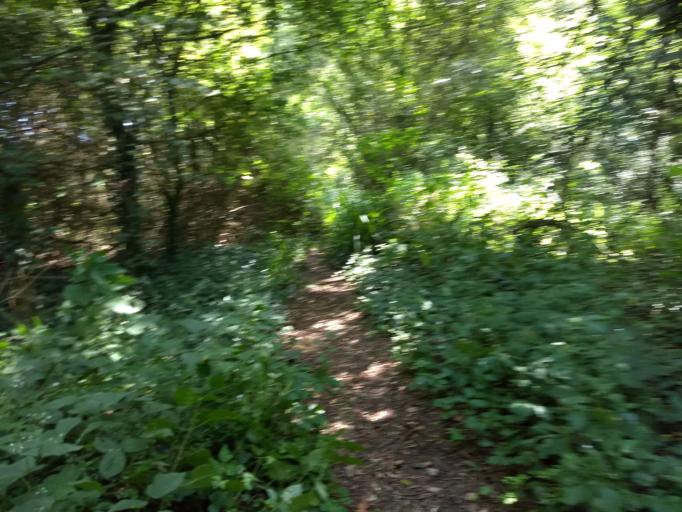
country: GB
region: England
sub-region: Isle of Wight
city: Northwood
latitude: 50.7265
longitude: -1.3443
